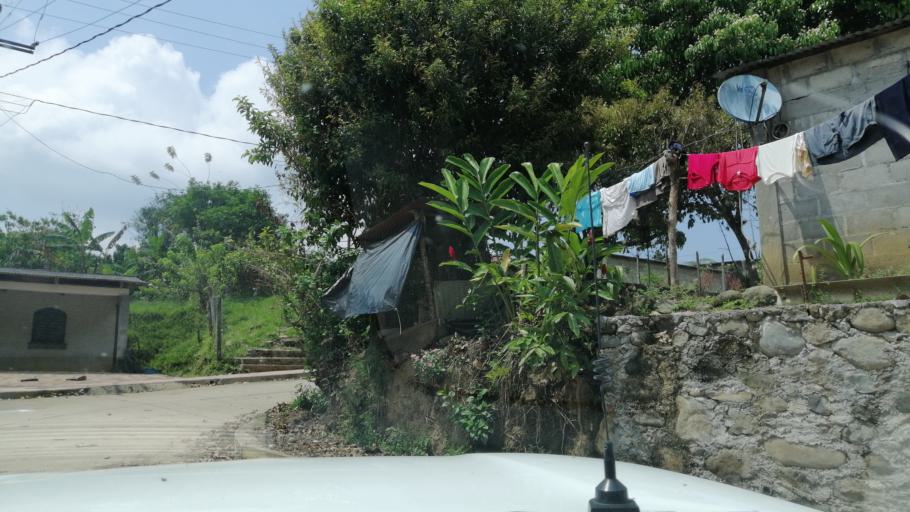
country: MX
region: Chiapas
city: Ostuacan
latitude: 17.3643
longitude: -93.3266
